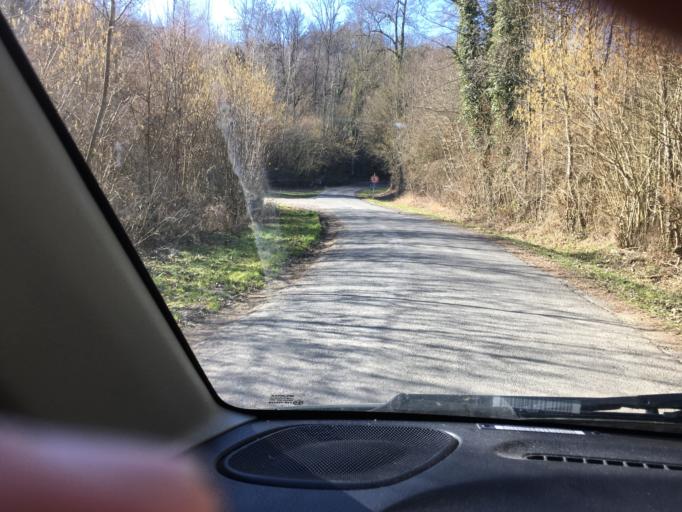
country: BE
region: Wallonia
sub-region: Province de Namur
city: Doische
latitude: 50.1177
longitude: 4.7339
